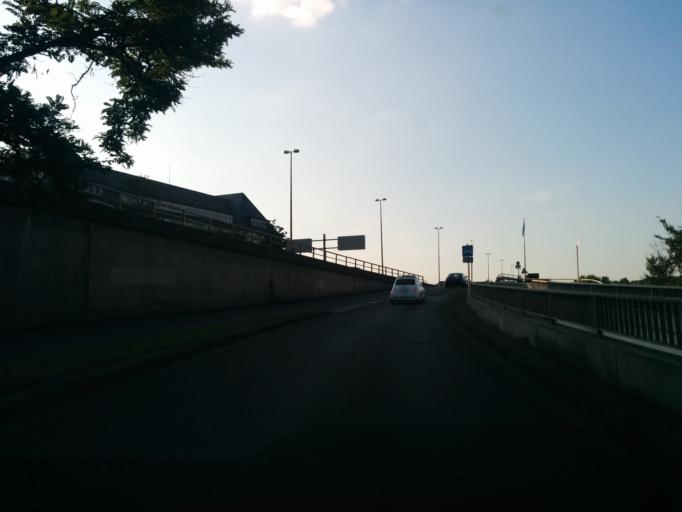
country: DE
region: Rheinland-Pfalz
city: Koblenz
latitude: 50.3616
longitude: 7.5883
